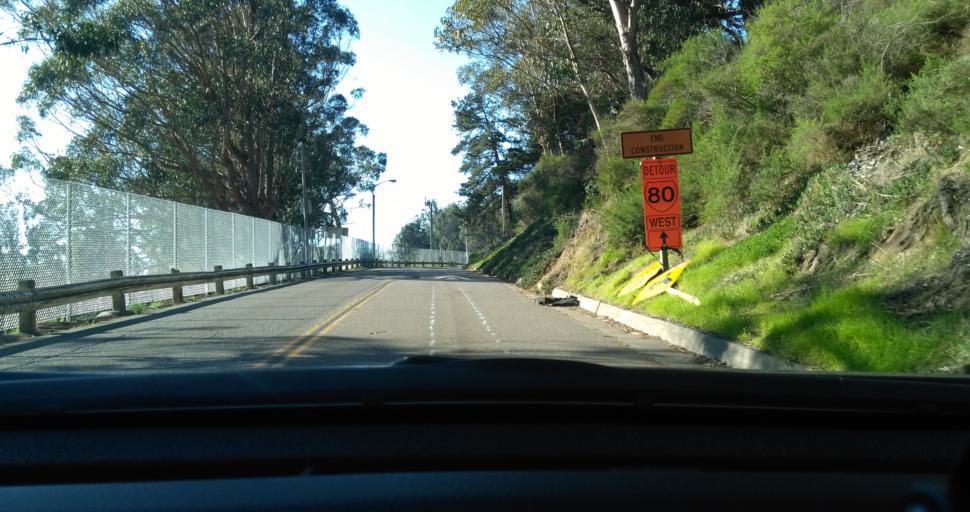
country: US
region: California
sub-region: San Francisco County
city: San Francisco
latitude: 37.8087
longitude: -122.3646
